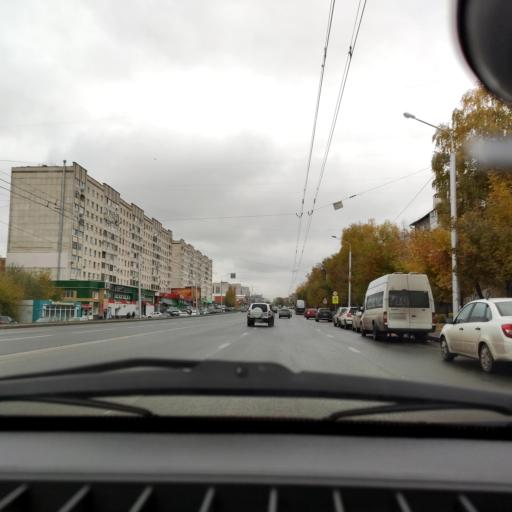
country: RU
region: Bashkortostan
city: Ufa
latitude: 54.7804
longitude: 56.0368
